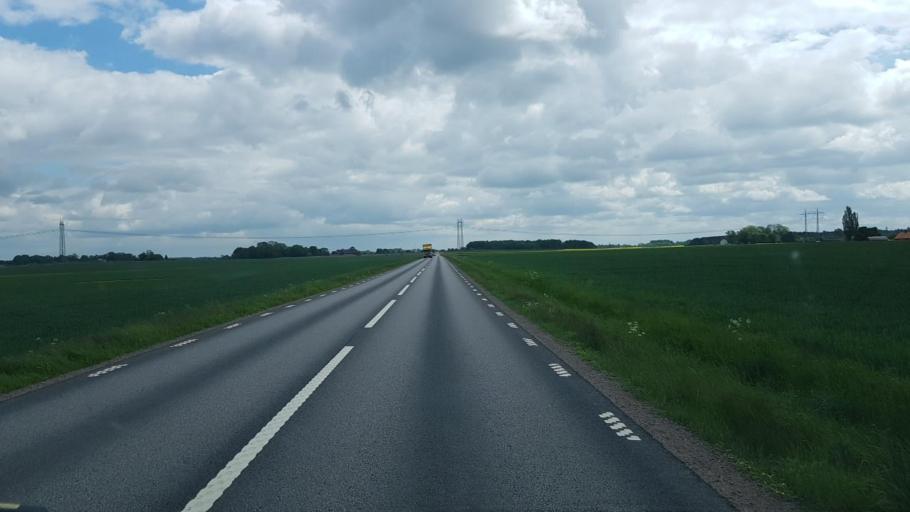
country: SE
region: OEstergoetland
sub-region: Motala Kommun
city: Borensberg
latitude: 58.5101
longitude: 15.1956
